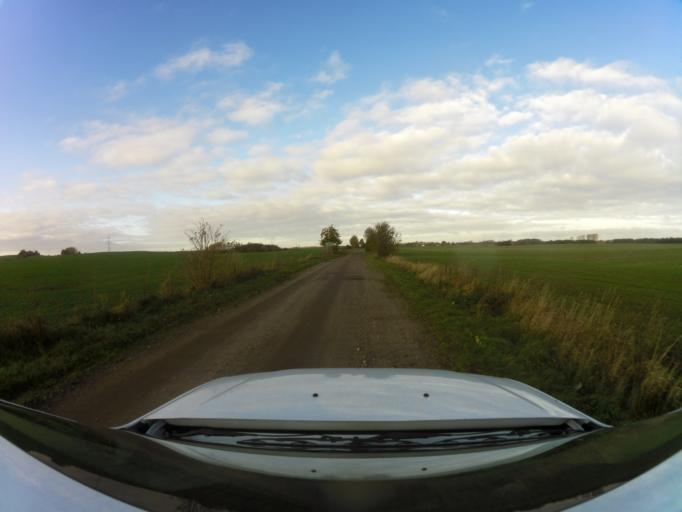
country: PL
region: West Pomeranian Voivodeship
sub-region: Powiat gryficki
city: Trzebiatow
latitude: 54.0515
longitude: 15.1931
